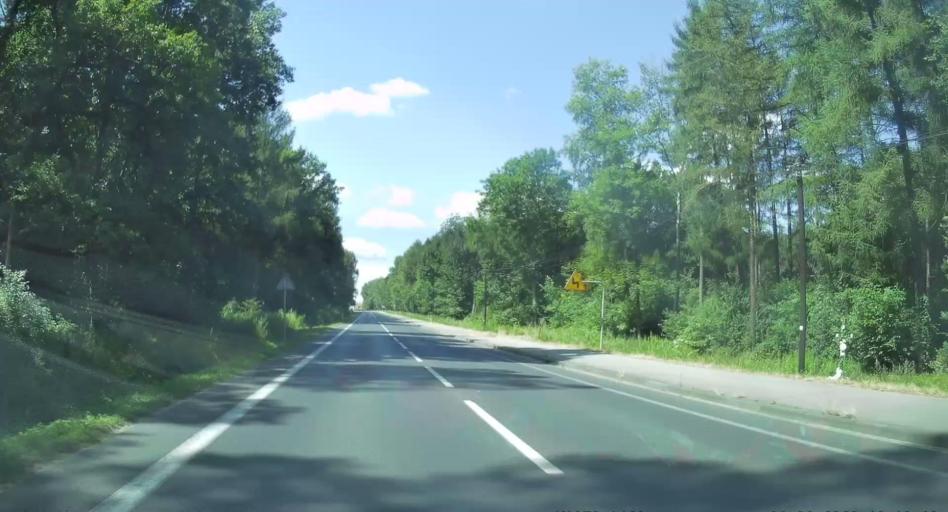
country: PL
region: Subcarpathian Voivodeship
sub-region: Powiat debicki
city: Brzeznica
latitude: 50.0972
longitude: 21.4718
